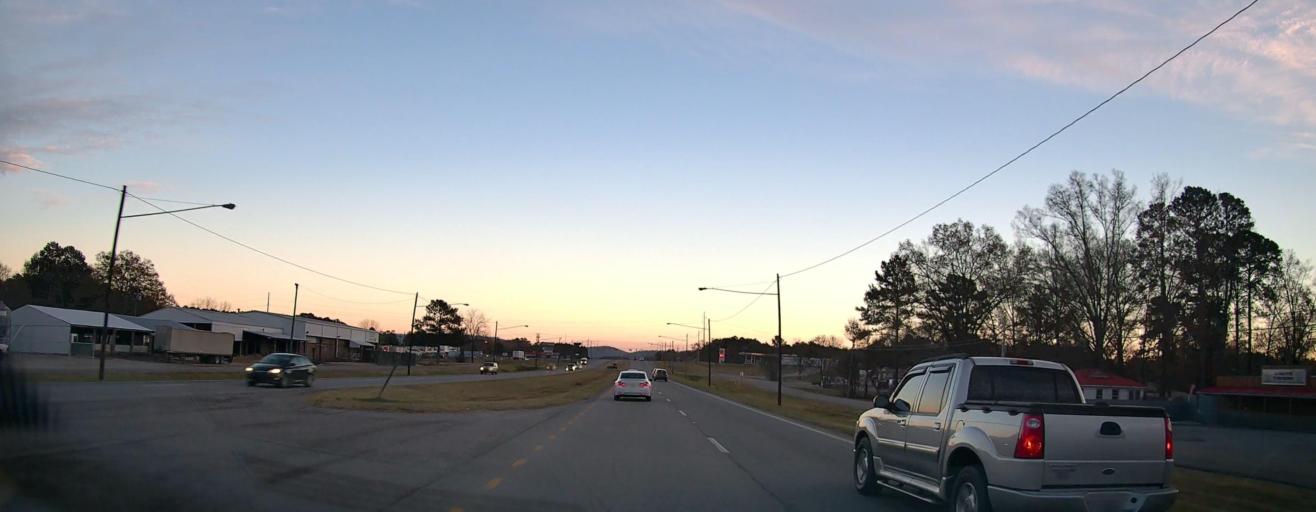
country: US
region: Alabama
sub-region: Etowah County
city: Glencoe
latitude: 33.9770
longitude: -85.9541
